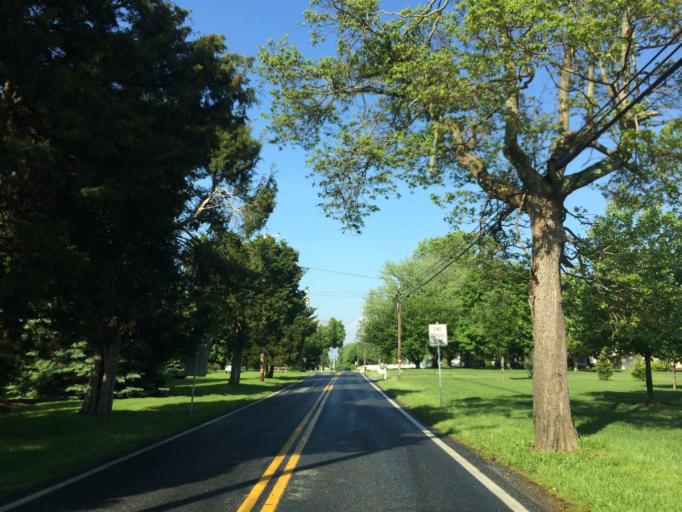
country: US
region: Maryland
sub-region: Howard County
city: Highland
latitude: 39.2668
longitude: -76.9758
